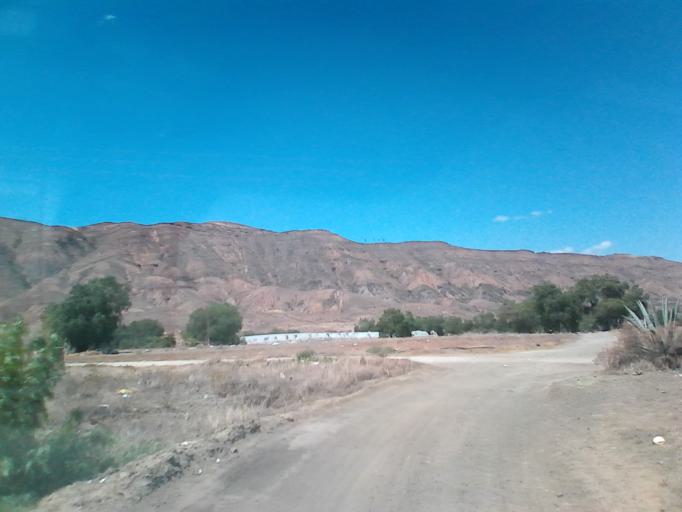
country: CO
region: Boyaca
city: Sachica
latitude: 5.5700
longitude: -73.5444
